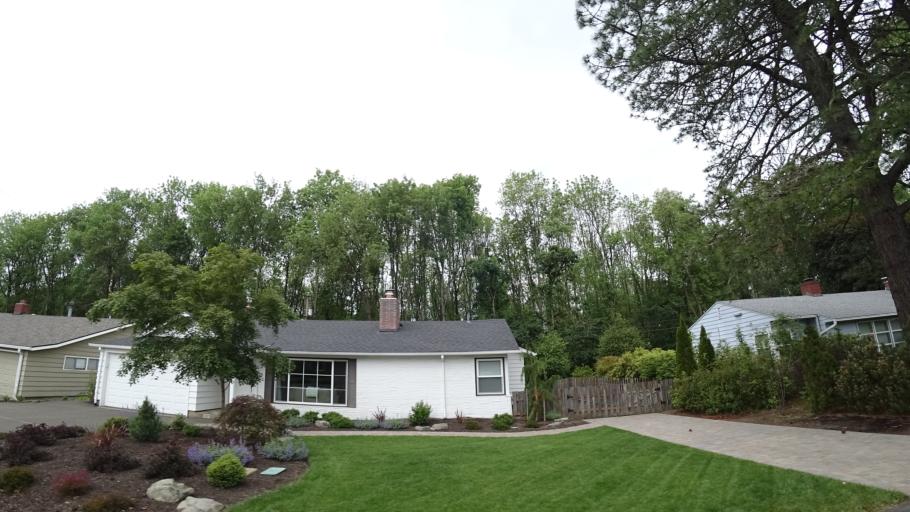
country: US
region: Oregon
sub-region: Washington County
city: Raleigh Hills
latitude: 45.4834
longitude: -122.7772
